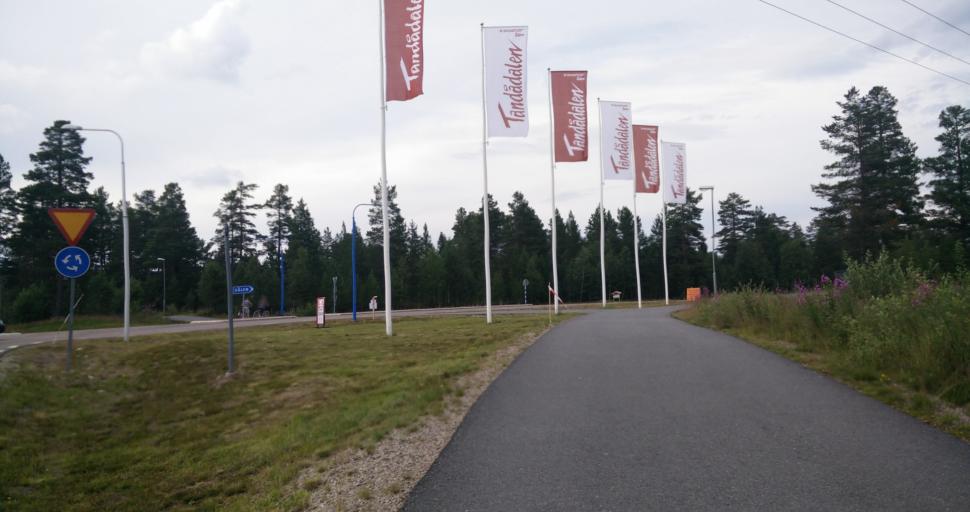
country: NO
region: Hedmark
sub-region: Trysil
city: Innbygda
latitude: 61.1795
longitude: 12.9926
